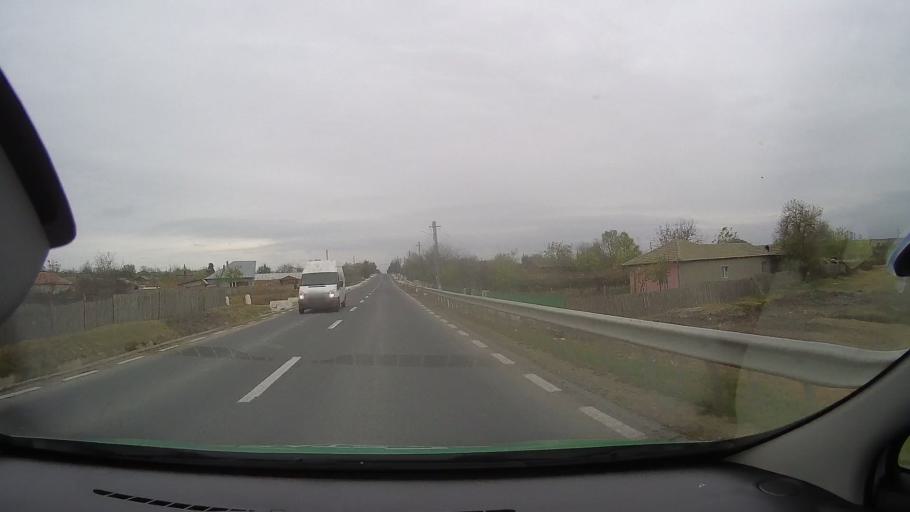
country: RO
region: Constanta
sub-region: Comuna Nicolae Balcescu
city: Dorobantu
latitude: 44.4126
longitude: 28.3206
